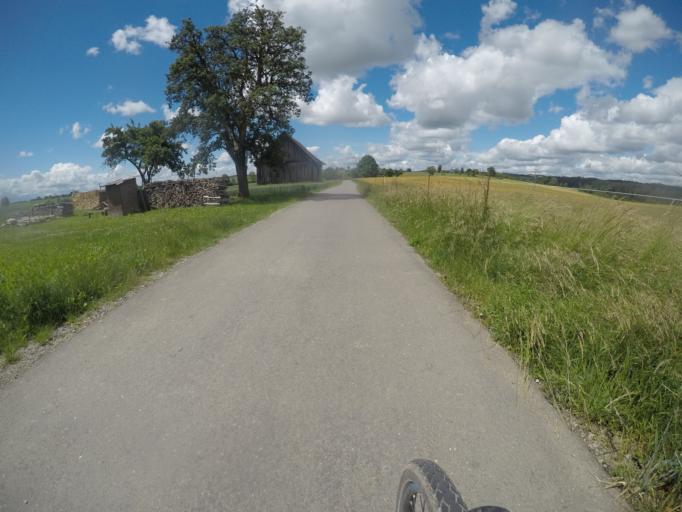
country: DE
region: Baden-Wuerttemberg
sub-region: Karlsruhe Region
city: Horb am Neckar
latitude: 48.4653
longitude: 8.7077
